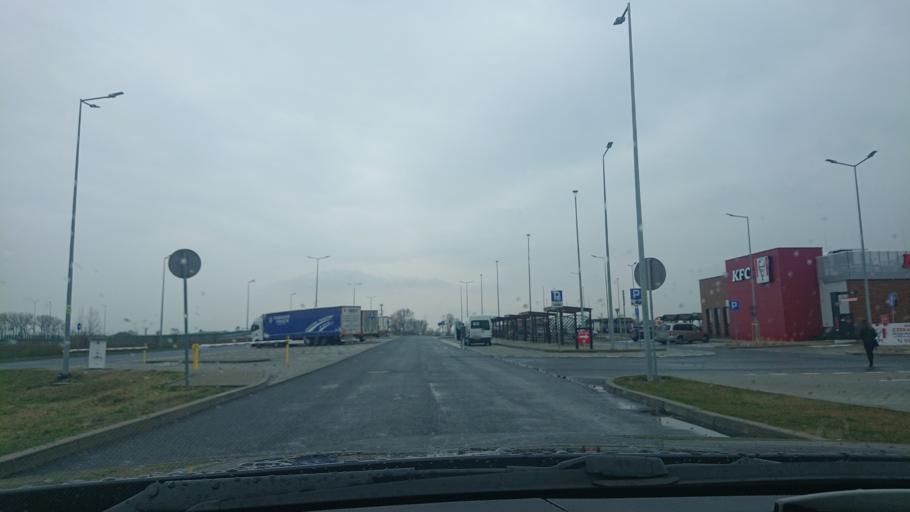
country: PL
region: Greater Poland Voivodeship
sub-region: Powiat gnieznienski
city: Lubowo
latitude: 52.5086
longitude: 17.4714
